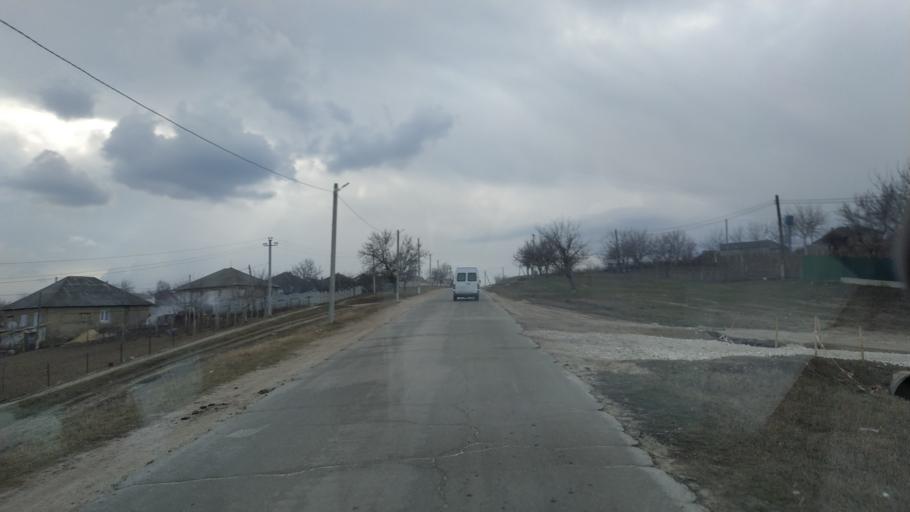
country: MD
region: Anenii Noi
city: Anenii Noi
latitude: 46.9053
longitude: 29.3210
